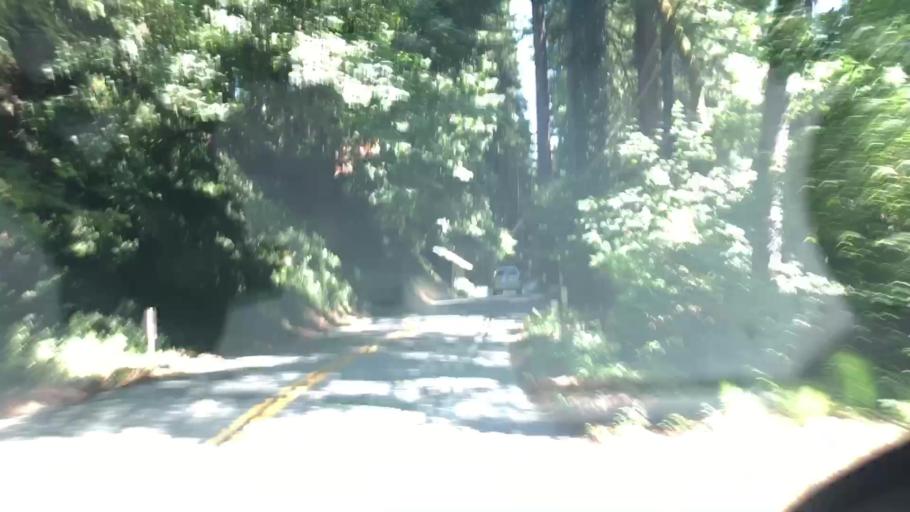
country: US
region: California
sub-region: Santa Cruz County
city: Corralitos
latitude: 37.0196
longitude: -121.8183
